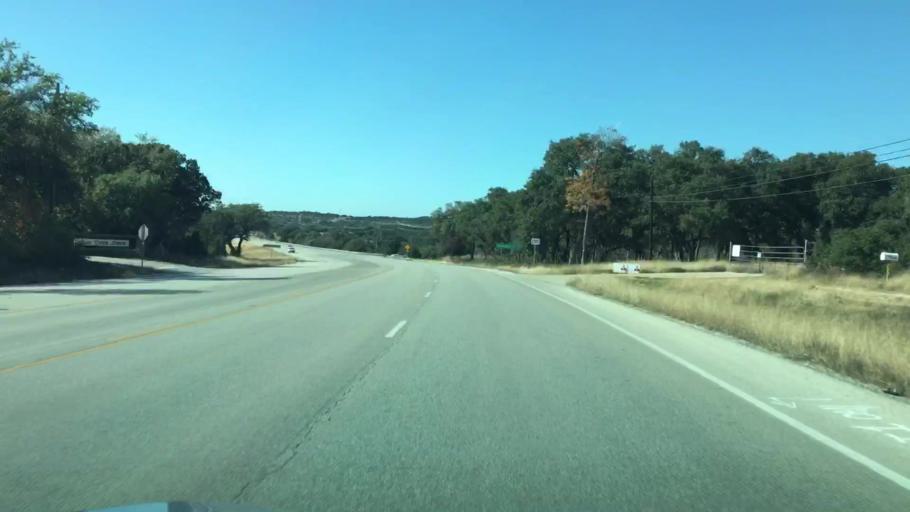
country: US
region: Texas
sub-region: Hays County
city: Dripping Springs
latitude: 30.2069
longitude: -98.1394
